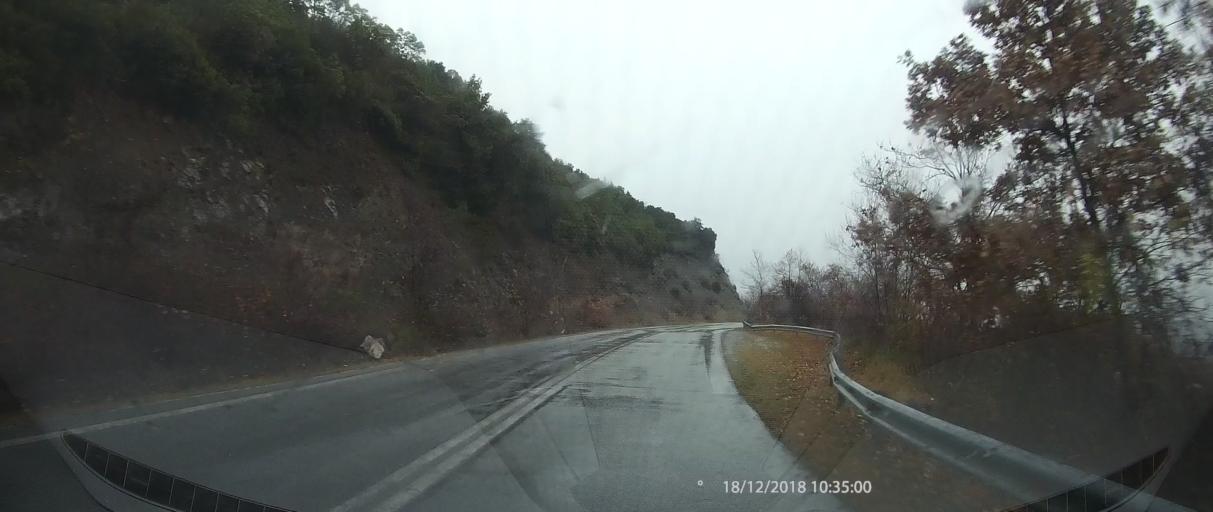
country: GR
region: Central Macedonia
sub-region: Nomos Pierias
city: Kato Milia
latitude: 40.2124
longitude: 22.3034
